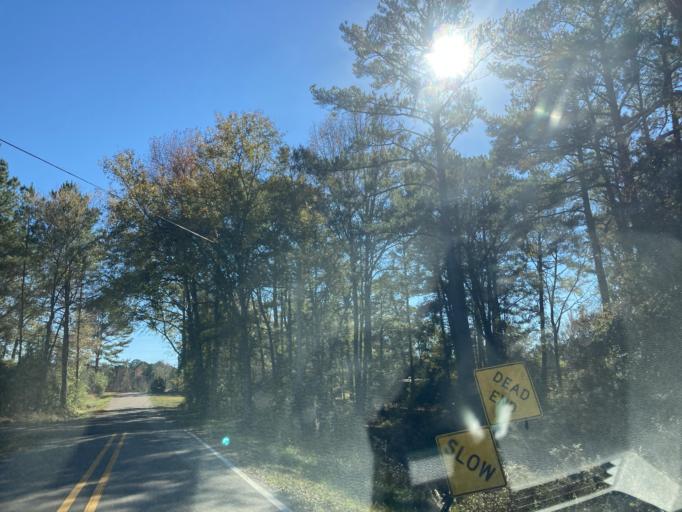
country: US
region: Mississippi
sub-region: Lamar County
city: Sumrall
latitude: 31.2851
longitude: -89.6453
